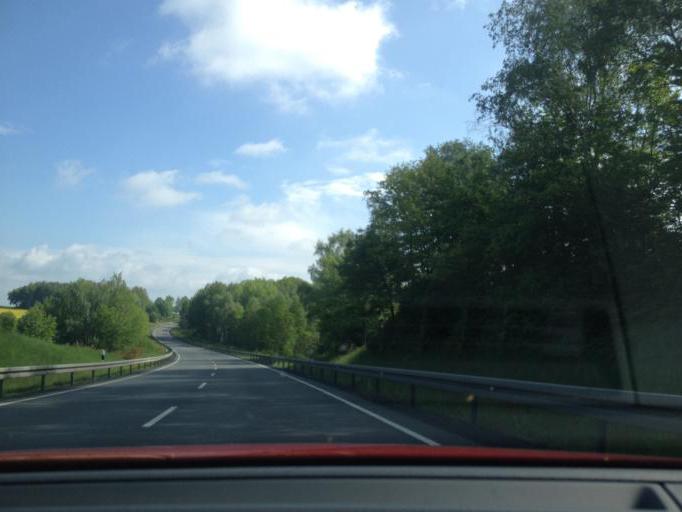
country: DE
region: Bavaria
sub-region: Upper Franconia
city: Arzberg
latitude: 50.0372
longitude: 12.1584
